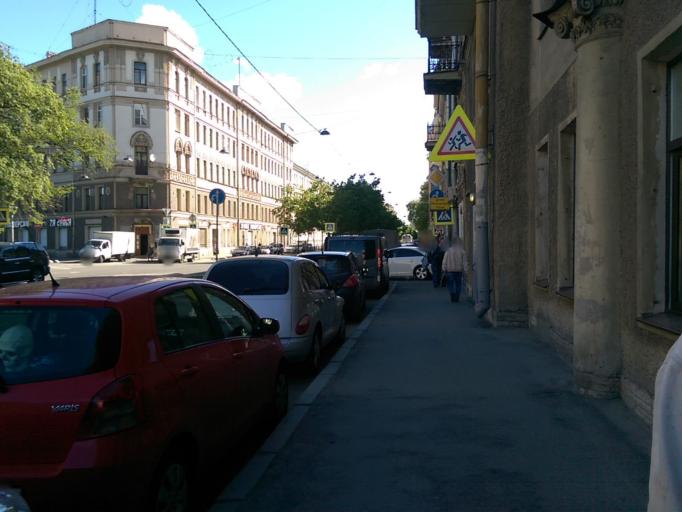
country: RU
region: St.-Petersburg
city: Saint Petersburg
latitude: 59.9115
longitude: 30.3206
